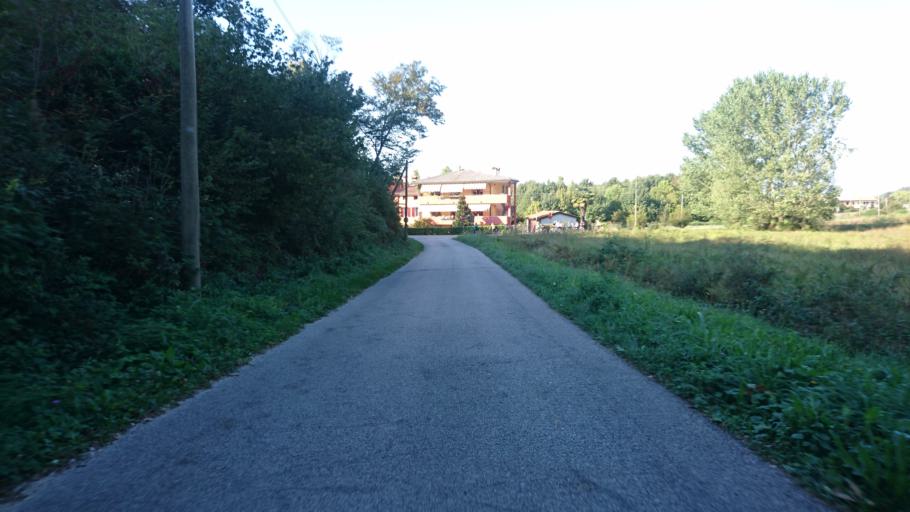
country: IT
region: Veneto
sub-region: Provincia di Padova
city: Torreglia
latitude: 45.3205
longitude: 11.7476
